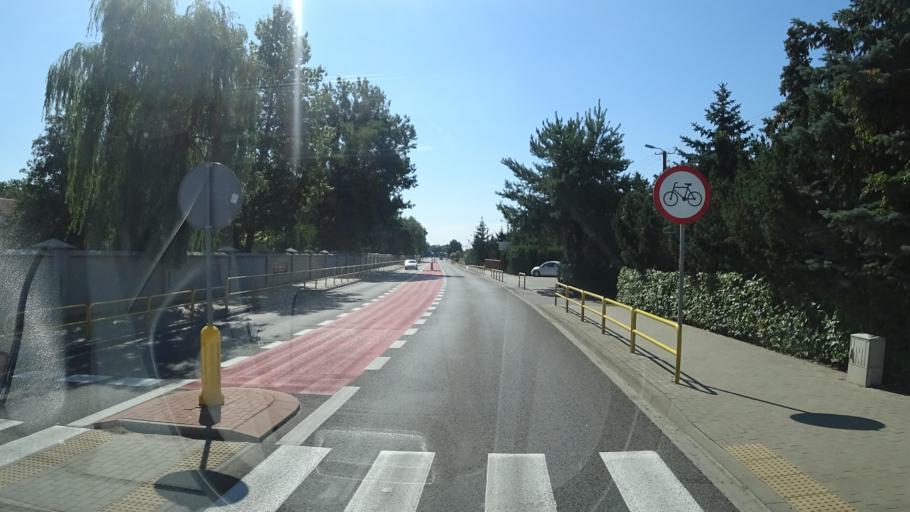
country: PL
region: Greater Poland Voivodeship
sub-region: Powiat koninski
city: Slesin
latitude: 52.3455
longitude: 18.2992
